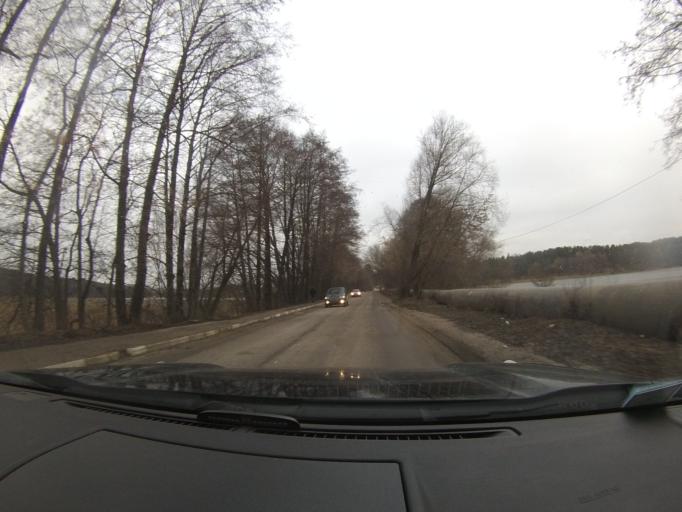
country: RU
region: Moskovskaya
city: Peski
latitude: 55.2628
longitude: 38.7611
